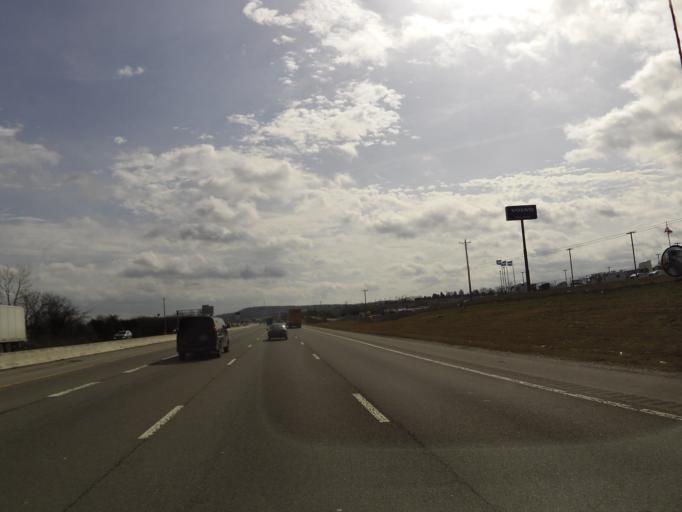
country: US
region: Tennessee
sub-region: Rutherford County
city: La Vergne
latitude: 36.0043
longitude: -86.6095
